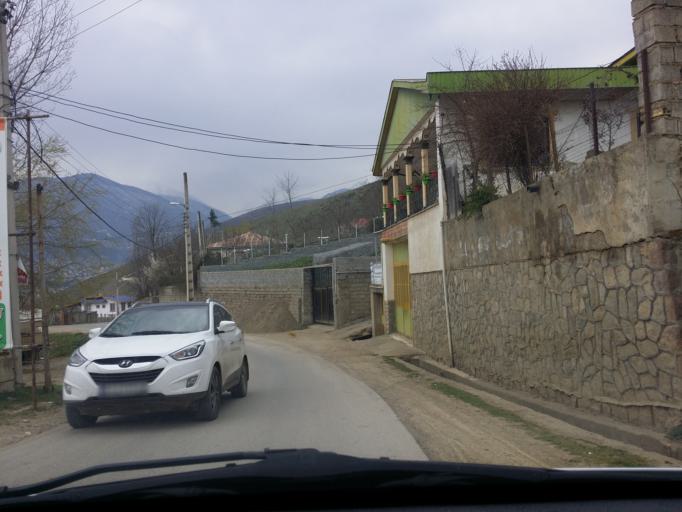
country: IR
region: Mazandaran
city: `Abbasabad
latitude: 36.5311
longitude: 51.1603
